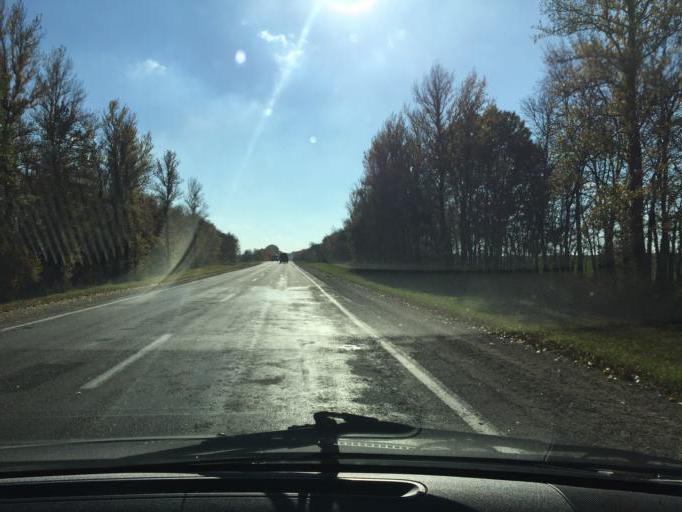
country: BY
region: Minsk
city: Salihorsk
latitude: 52.8959
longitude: 27.4740
